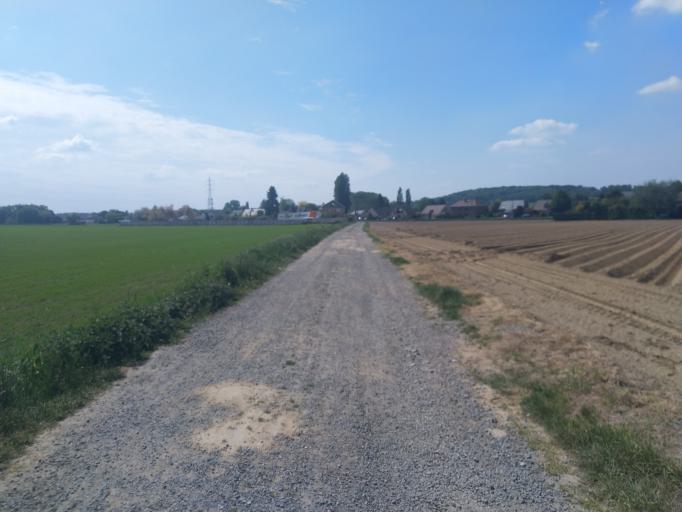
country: BE
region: Wallonia
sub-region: Province du Hainaut
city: Chasse Royale
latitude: 50.4323
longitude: 4.0048
